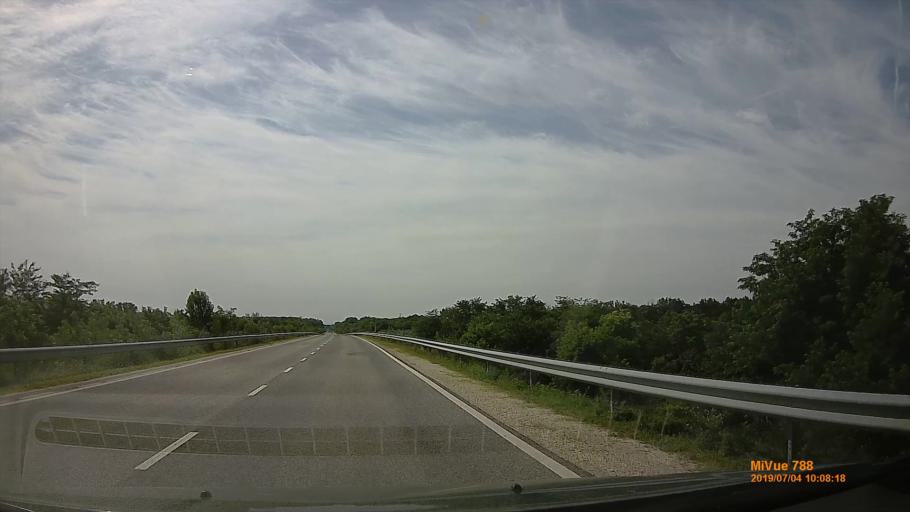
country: HU
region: Komarom-Esztergom
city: Komarom
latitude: 47.7424
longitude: 18.0917
